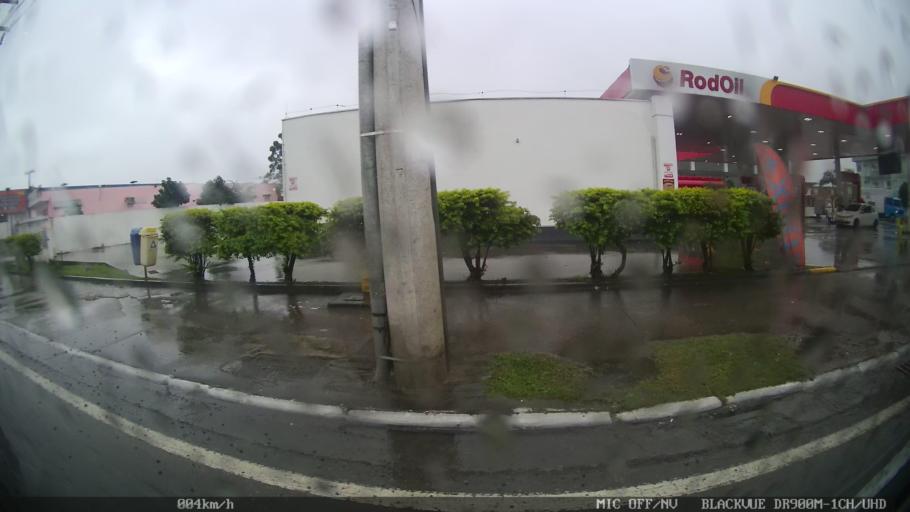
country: BR
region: Santa Catarina
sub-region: Itajai
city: Itajai
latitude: -26.8847
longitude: -48.6960
